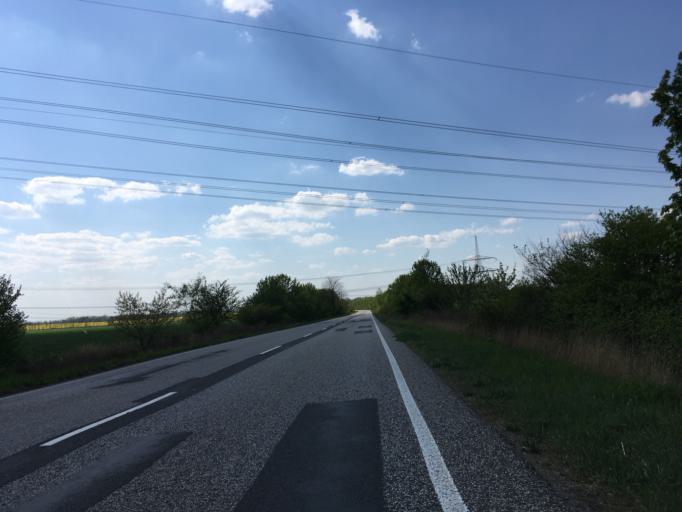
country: DE
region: Brandenburg
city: Werneuchen
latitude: 52.6112
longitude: 13.6666
